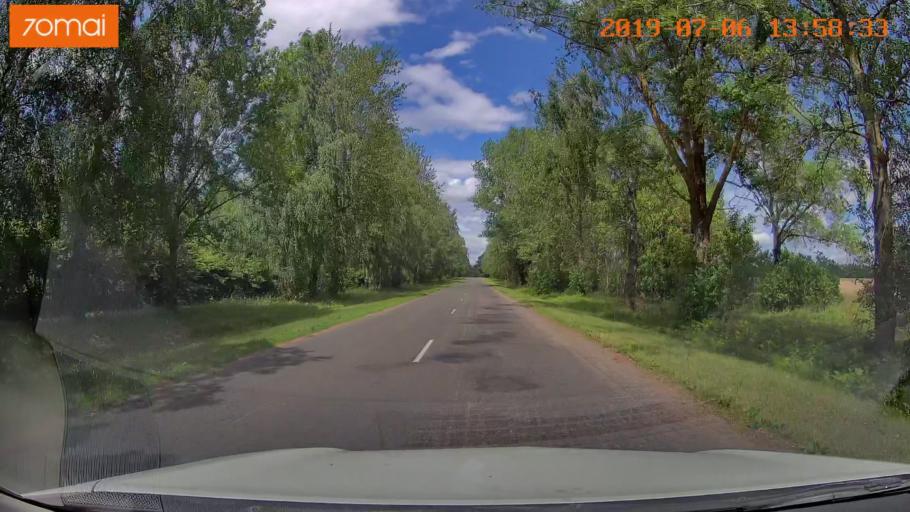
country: BY
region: Minsk
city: Ivyanyets
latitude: 53.7853
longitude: 26.8094
